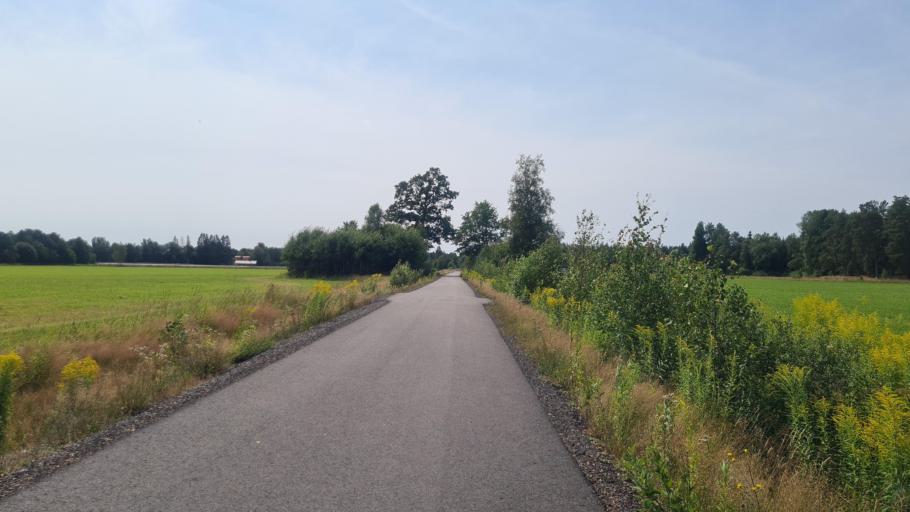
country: SE
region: Kronoberg
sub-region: Ljungby Kommun
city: Ljungby
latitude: 56.8553
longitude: 13.9731
